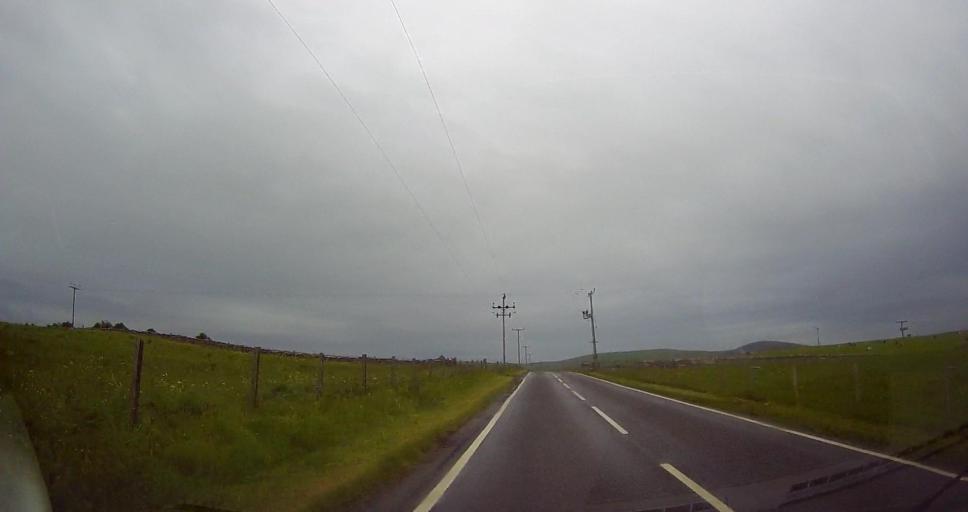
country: GB
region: Scotland
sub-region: Orkney Islands
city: Stromness
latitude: 59.0238
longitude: -3.2960
